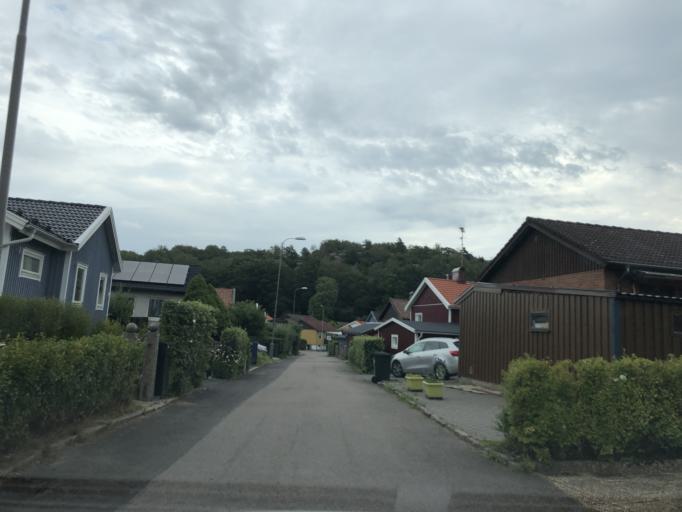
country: SE
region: Vaestra Goetaland
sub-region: Goteborg
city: Majorna
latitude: 57.7269
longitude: 11.9158
